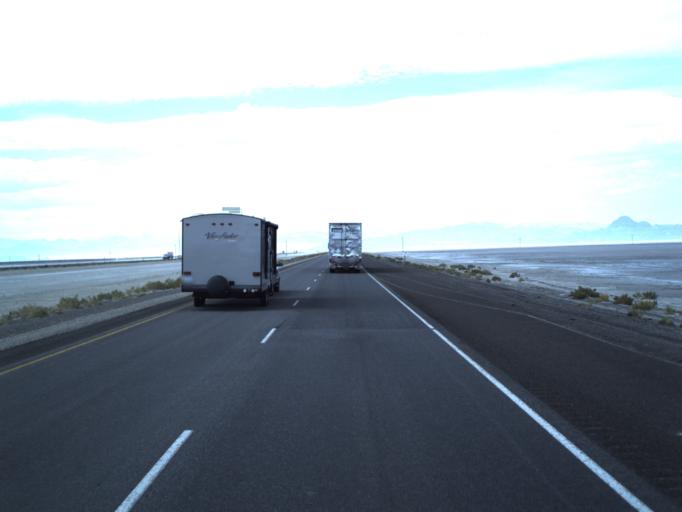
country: US
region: Utah
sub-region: Tooele County
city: Wendover
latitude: 40.7374
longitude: -113.7553
